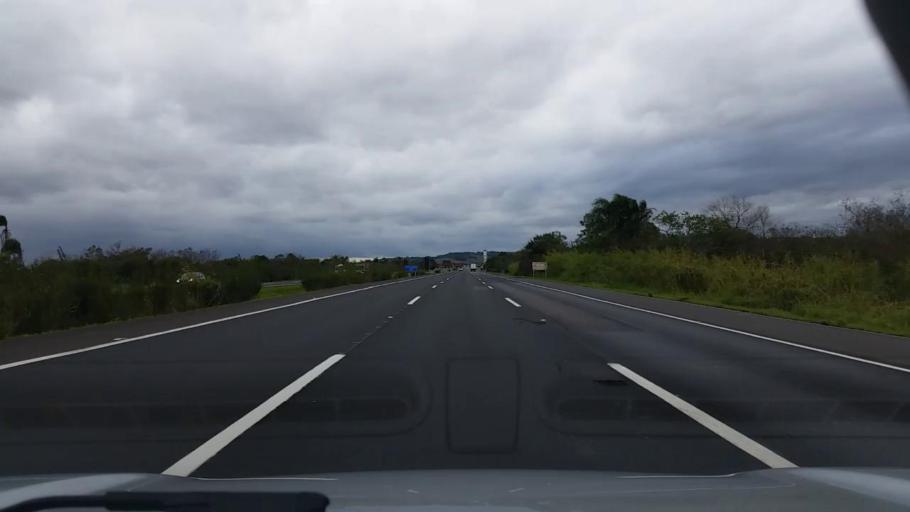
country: BR
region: Rio Grande do Sul
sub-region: Osorio
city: Osorio
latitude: -29.8822
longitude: -50.4380
